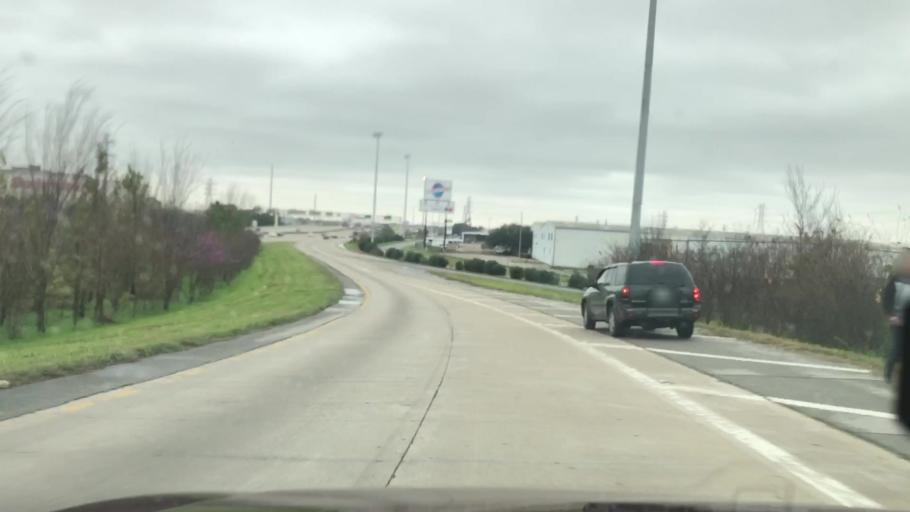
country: US
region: Texas
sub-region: Harris County
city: Jacinto City
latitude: 29.7766
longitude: -95.2659
